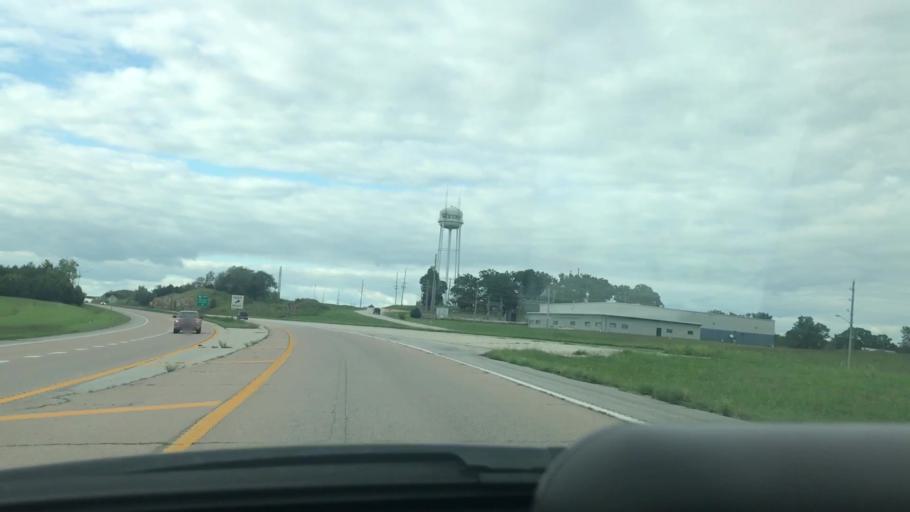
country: US
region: Missouri
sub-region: Benton County
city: Warsaw
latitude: 38.2456
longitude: -93.3603
